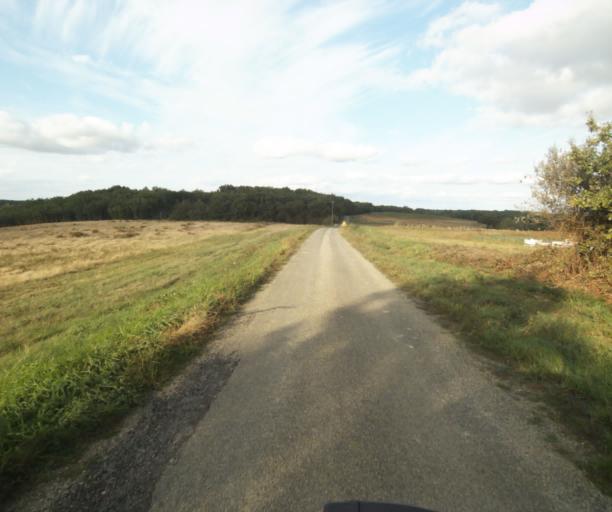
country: FR
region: Midi-Pyrenees
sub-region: Departement de la Haute-Garonne
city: Launac
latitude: 43.8010
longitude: 1.1169
